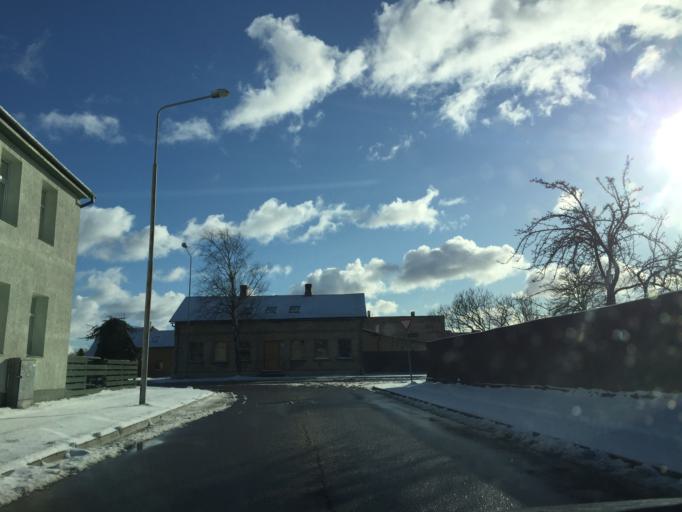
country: LV
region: Ventspils
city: Ventspils
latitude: 57.3859
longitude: 21.5576
